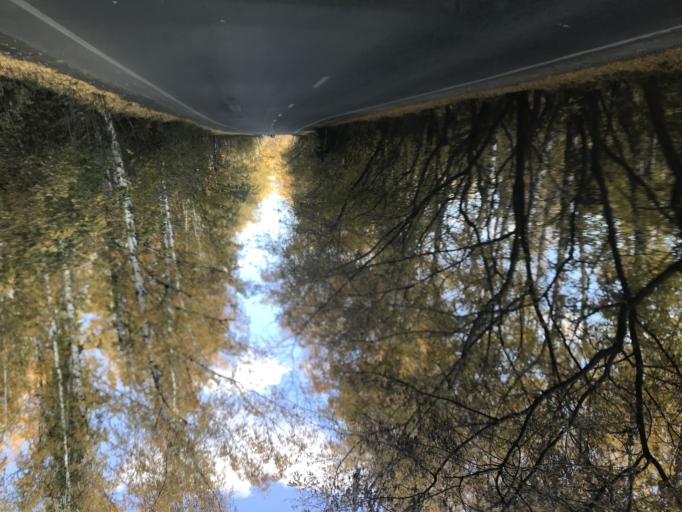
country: RU
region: Chelyabinsk
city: Dolgoderevenskoye
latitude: 55.2596
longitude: 61.3636
